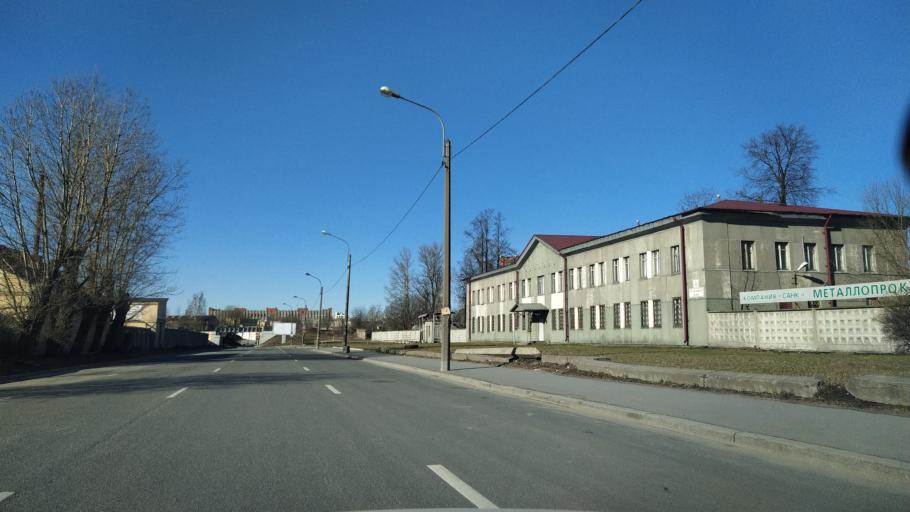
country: RU
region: St.-Petersburg
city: Centralniy
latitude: 59.9100
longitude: 30.3759
